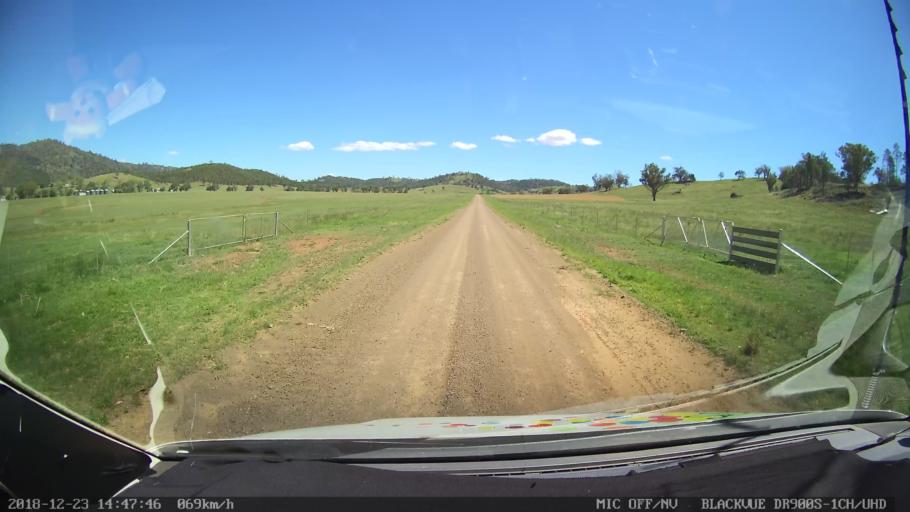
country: AU
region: New South Wales
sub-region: Tamworth Municipality
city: Manilla
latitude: -30.6562
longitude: 150.8726
